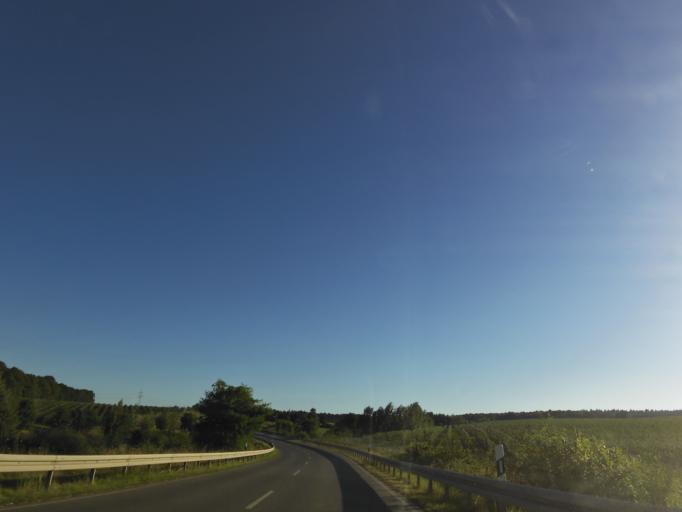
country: DE
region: Saxony
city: Kreischa
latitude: 50.9620
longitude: 13.7972
